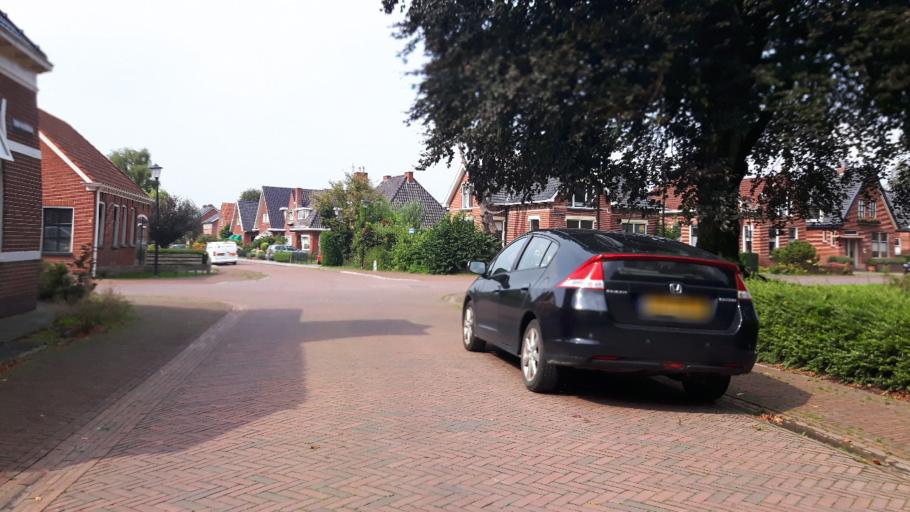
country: NL
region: Groningen
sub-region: Gemeente Bedum
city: Bedum
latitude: 53.3479
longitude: 6.6406
